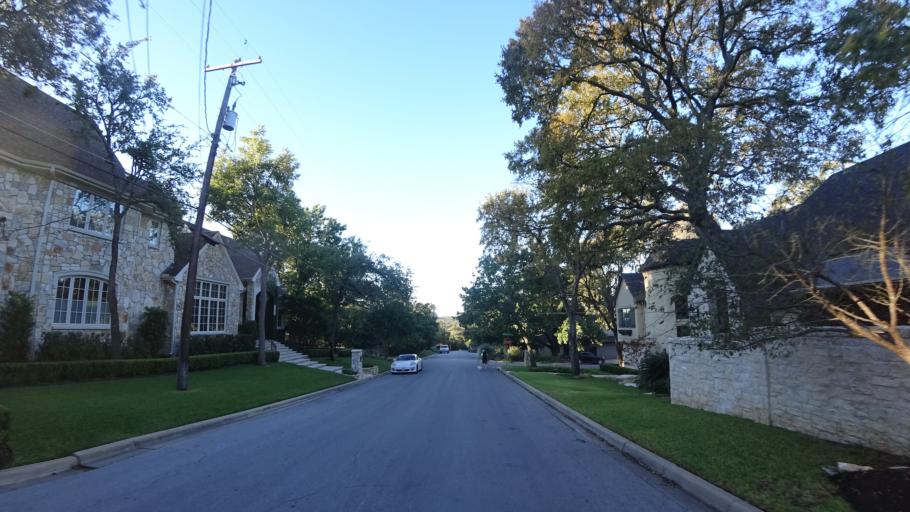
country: US
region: Texas
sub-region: Travis County
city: West Lake Hills
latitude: 30.3012
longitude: -97.7804
